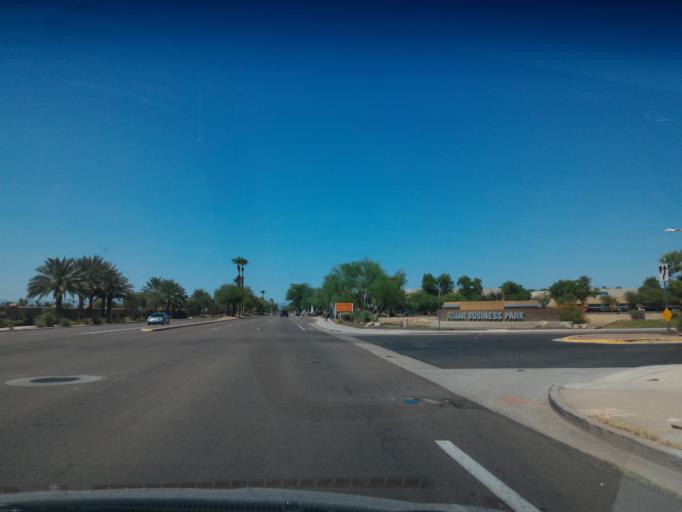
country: US
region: Arizona
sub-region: Maricopa County
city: Chandler
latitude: 33.3055
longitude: -111.9153
